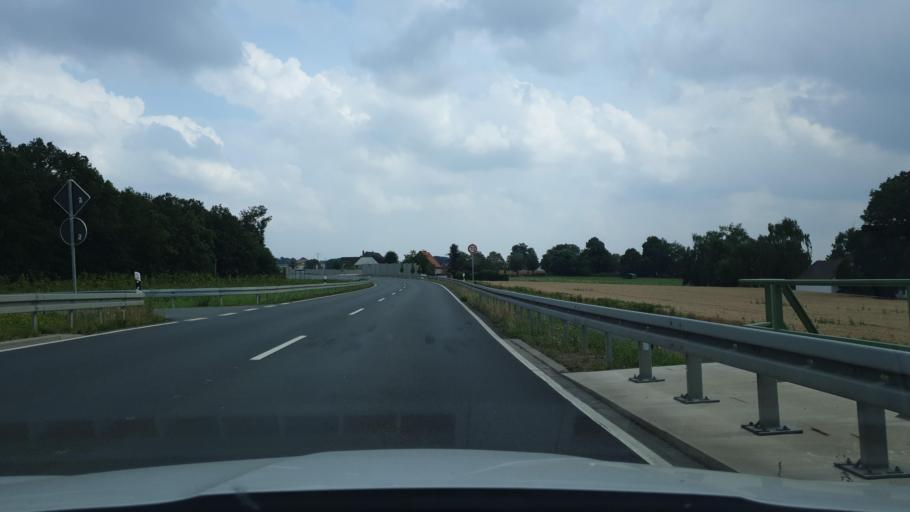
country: DE
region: North Rhine-Westphalia
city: Bad Oeynhausen
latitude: 52.1635
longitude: 8.7546
